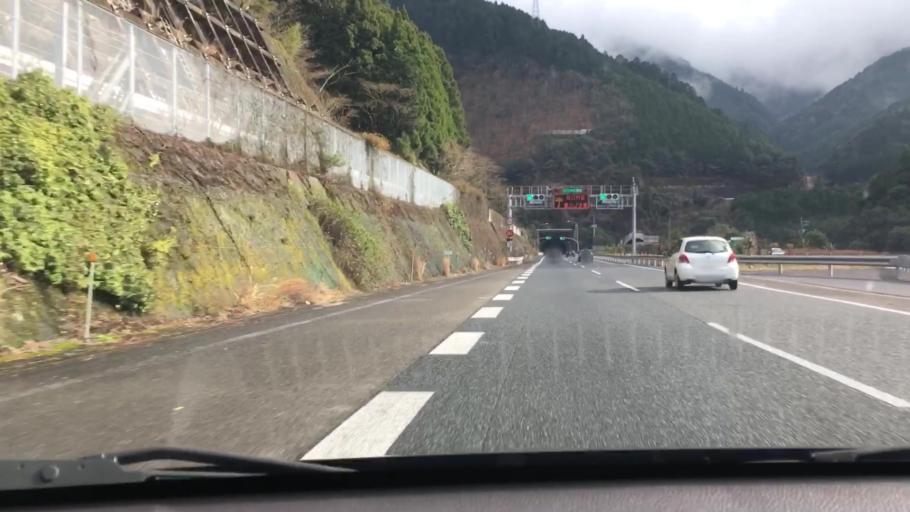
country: JP
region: Kumamoto
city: Yatsushiro
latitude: 32.3960
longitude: 130.7047
